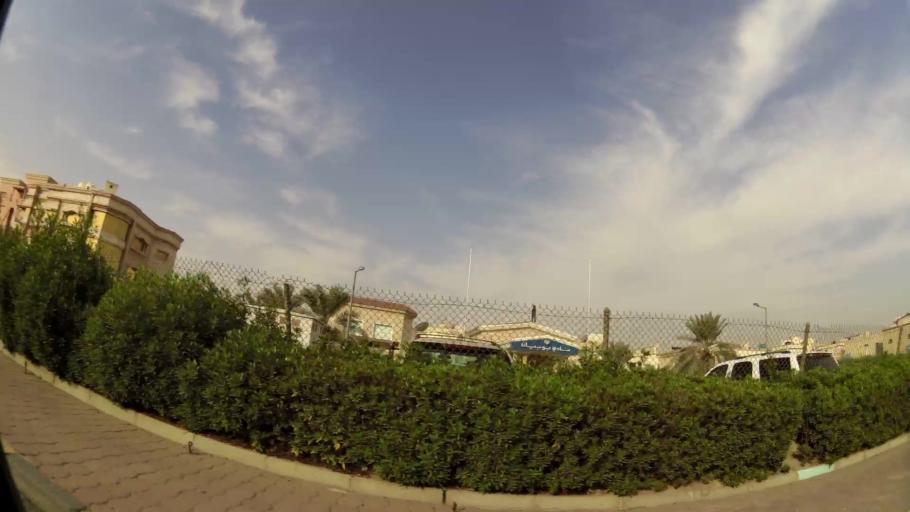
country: KW
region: Muhafazat Hawalli
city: Salwa
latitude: 29.3008
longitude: 48.0850
